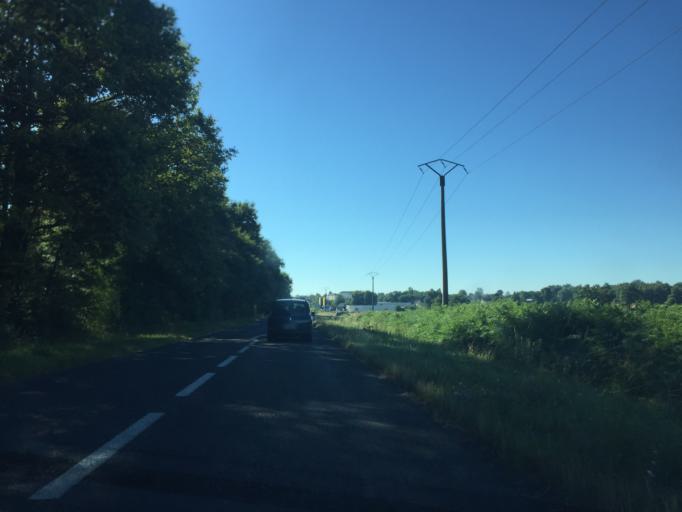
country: FR
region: Auvergne
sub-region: Departement de l'Allier
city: Dompierre-sur-Besbre
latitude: 46.5326
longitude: 3.6633
